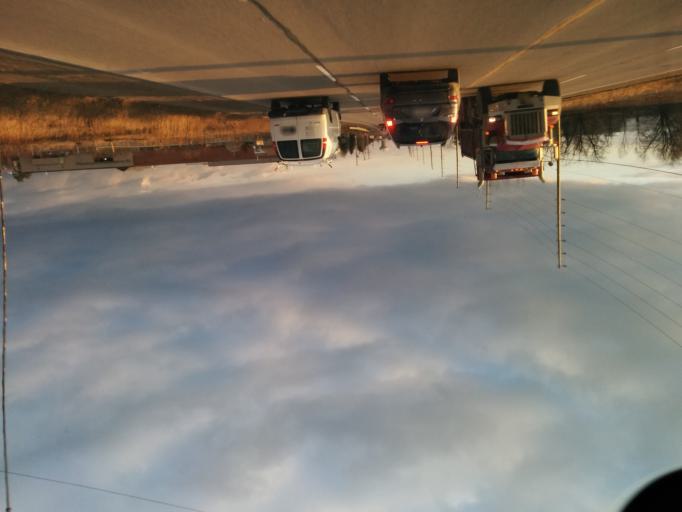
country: CA
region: Ontario
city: Brampton
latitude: 43.8553
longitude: -79.7283
